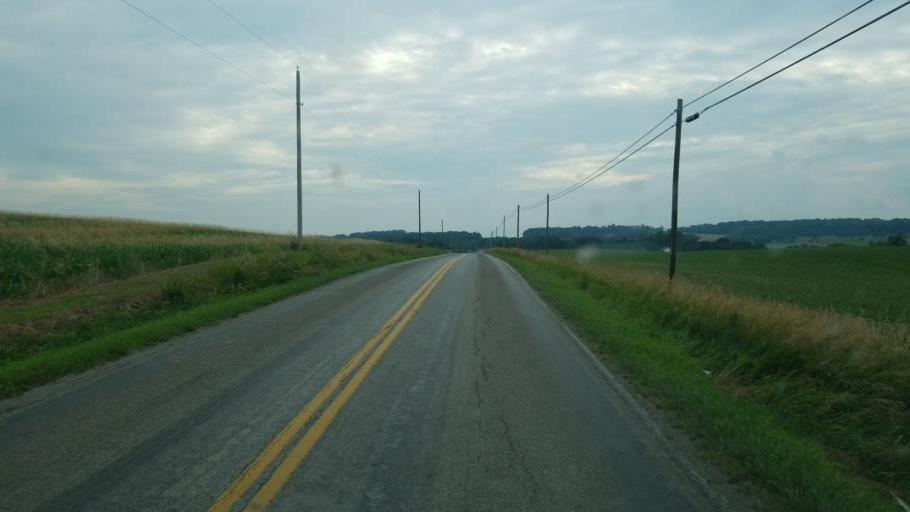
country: US
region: Ohio
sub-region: Wayne County
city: Apple Creek
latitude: 40.7557
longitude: -81.8093
